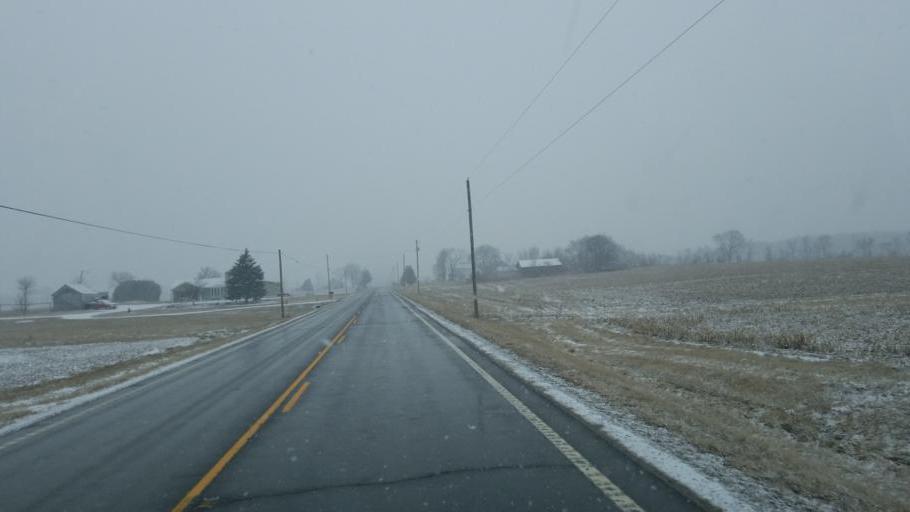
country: US
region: Ohio
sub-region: Defiance County
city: Hicksville
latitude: 41.3404
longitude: -84.7477
